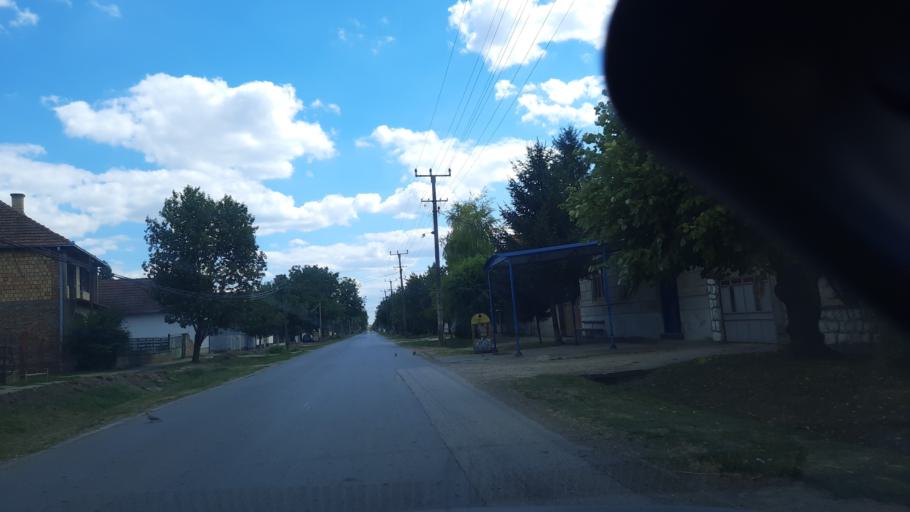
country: RS
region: Autonomna Pokrajina Vojvodina
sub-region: Sremski Okrug
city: Pecinci
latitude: 44.9322
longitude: 20.0071
